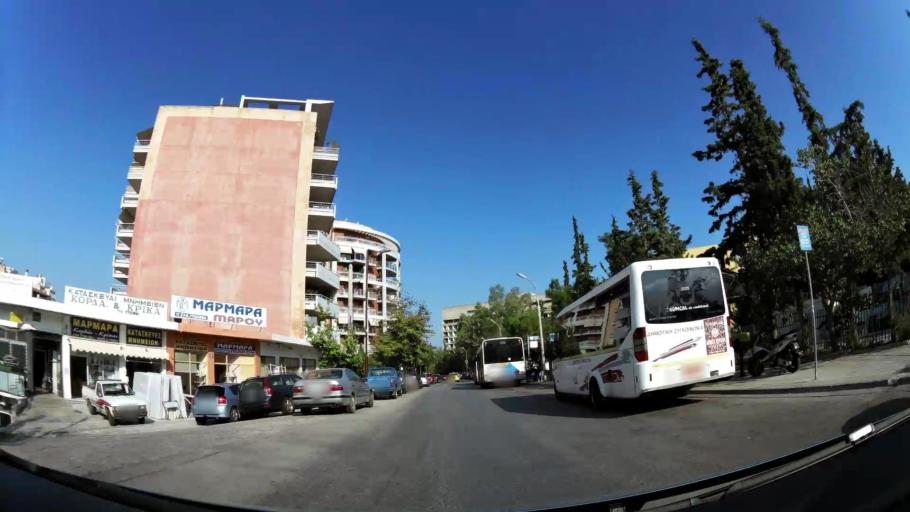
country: GR
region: Attica
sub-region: Nomos Attikis
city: Zografos
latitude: 37.9721
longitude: 23.7816
